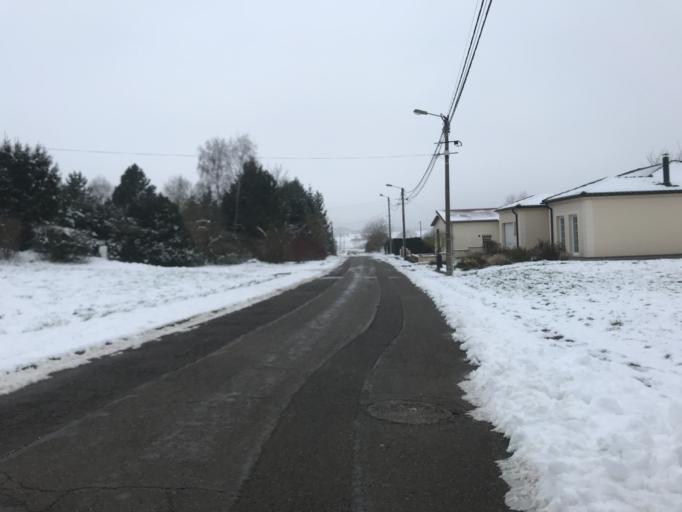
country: FR
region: Lorraine
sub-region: Departement de la Moselle
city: Russange
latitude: 49.4890
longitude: 5.9483
